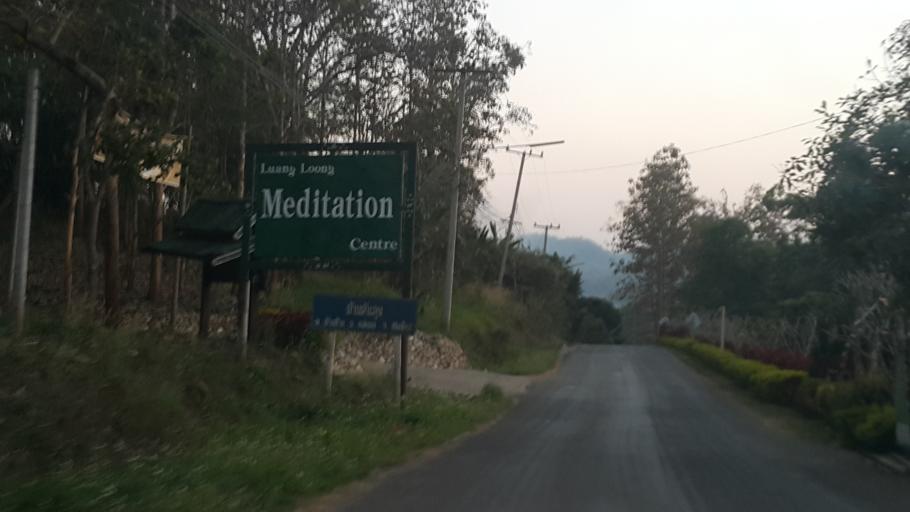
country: TH
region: Chiang Mai
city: Mae Taeng
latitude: 19.1549
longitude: 98.8592
